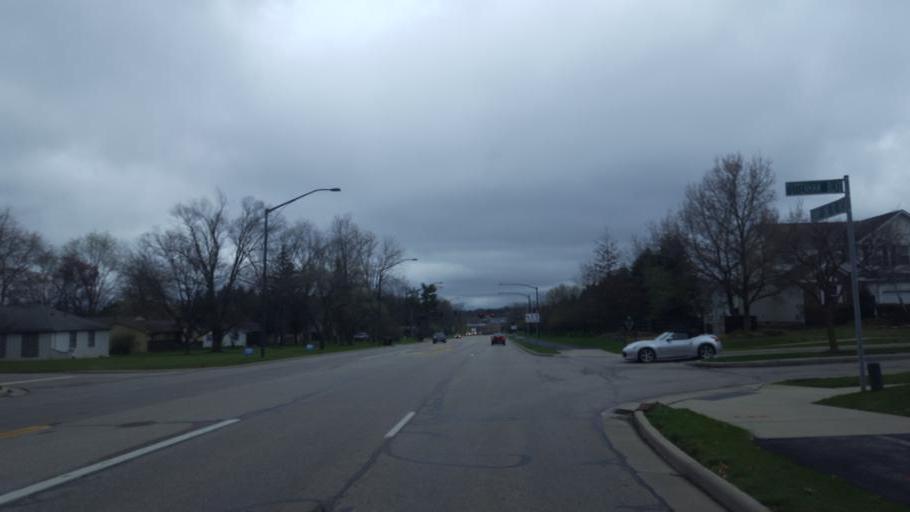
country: US
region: Ohio
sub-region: Franklin County
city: Westerville
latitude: 40.1381
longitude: -82.9592
